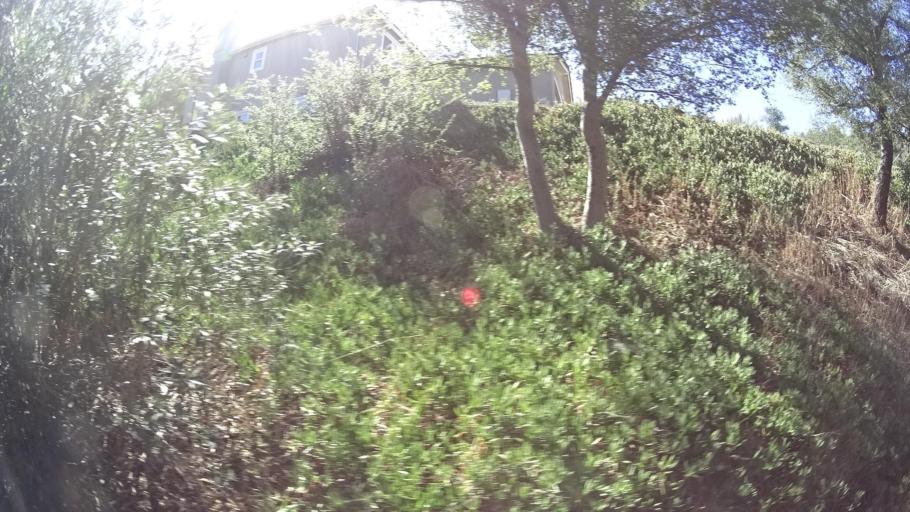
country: US
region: California
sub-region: San Diego County
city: Alpine
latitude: 32.8537
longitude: -116.7908
